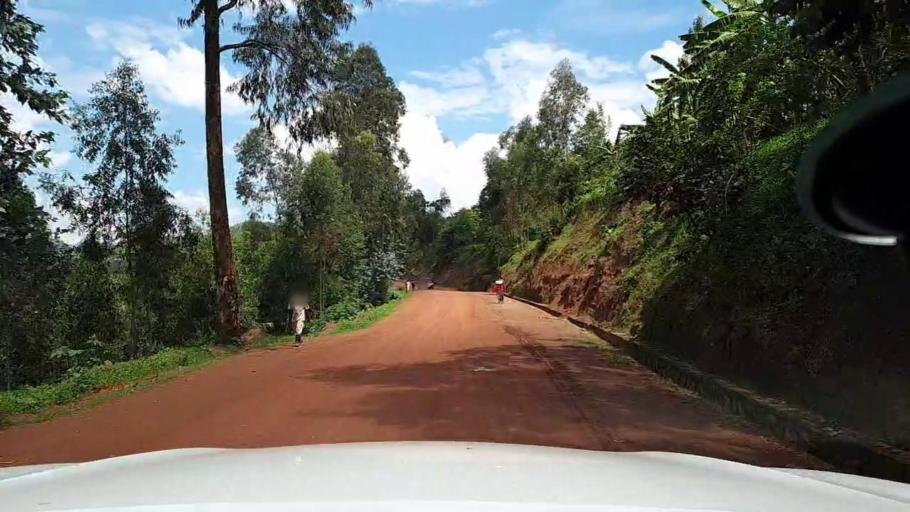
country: RW
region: Northern Province
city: Byumba
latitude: -1.7341
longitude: 29.8567
